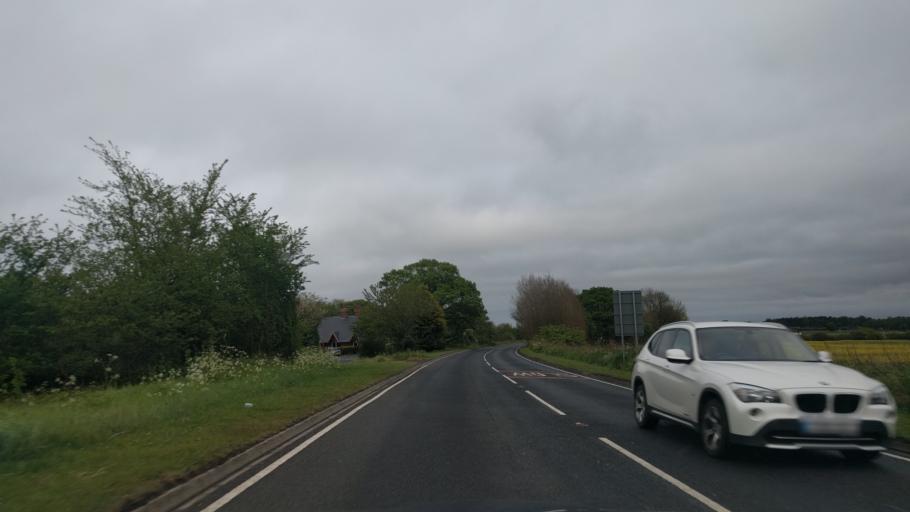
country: GB
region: England
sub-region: Northumberland
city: Pegswood
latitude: 55.1632
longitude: -1.6398
